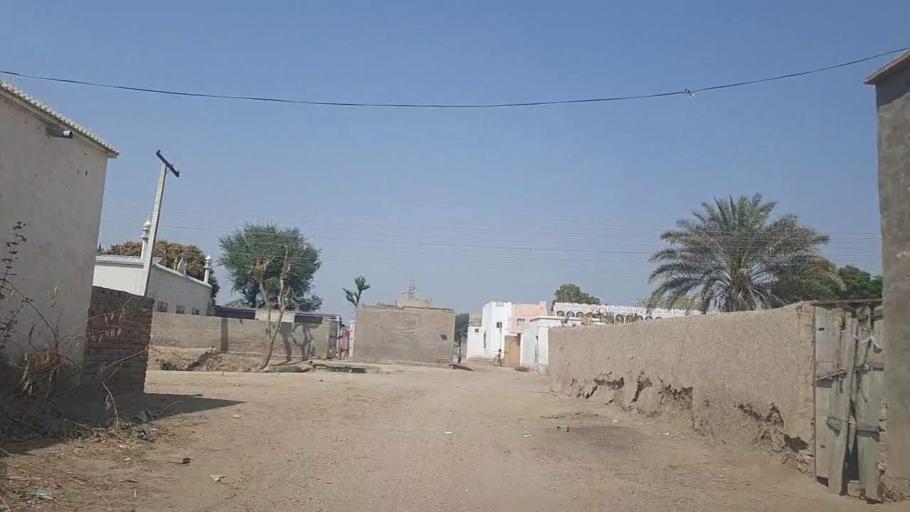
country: PK
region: Sindh
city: Naukot
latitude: 24.8411
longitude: 69.4174
